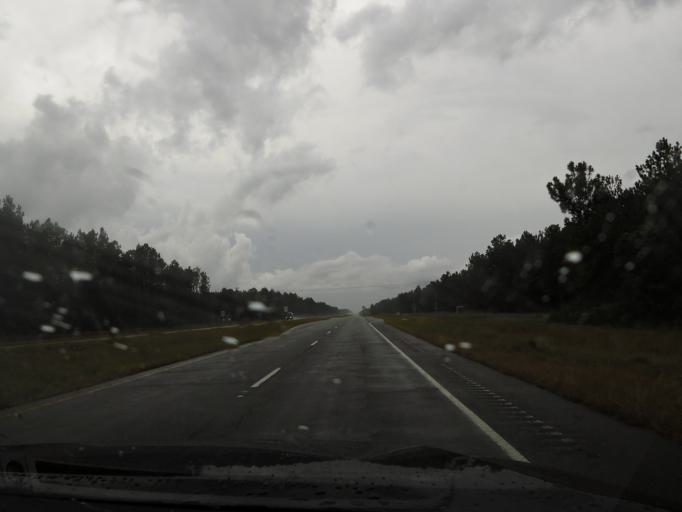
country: US
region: Georgia
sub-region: Wayne County
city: Jesup
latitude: 31.4549
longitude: -81.7027
